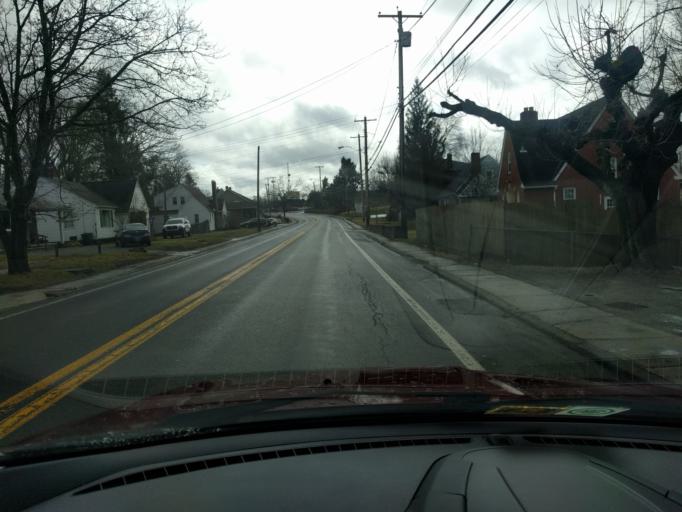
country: US
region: West Virginia
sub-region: Raleigh County
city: Mabscott
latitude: 37.7814
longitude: -81.2045
